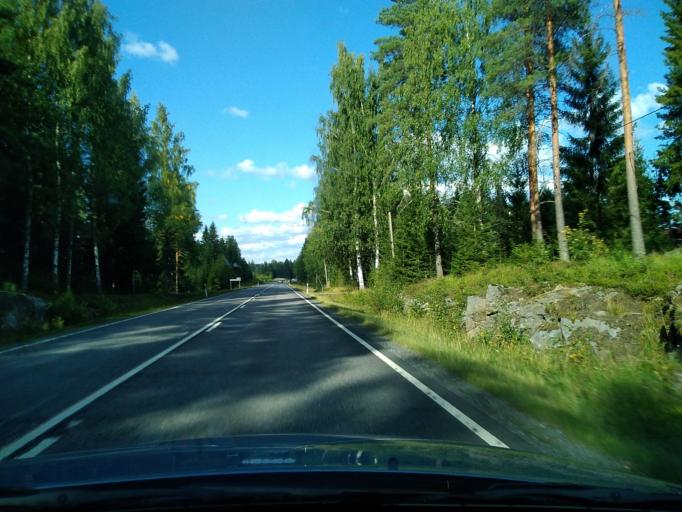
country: FI
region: Pirkanmaa
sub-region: Ylae-Pirkanmaa
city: Maenttae
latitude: 61.9727
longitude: 24.6038
